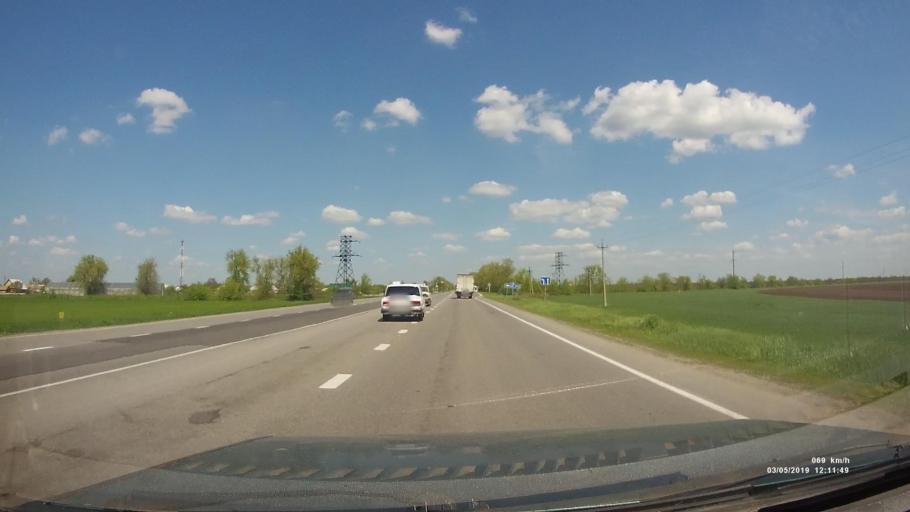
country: RU
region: Rostov
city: Bagayevskaya
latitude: 47.3147
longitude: 40.5416
